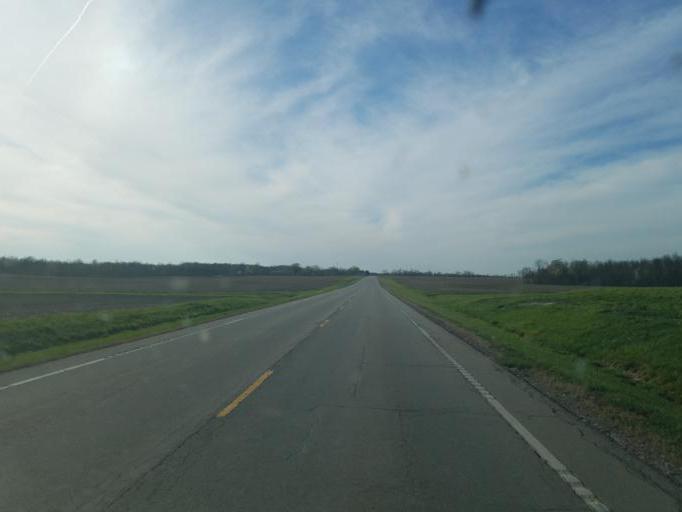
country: US
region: Ohio
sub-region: Huron County
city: New London
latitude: 41.0765
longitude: -82.4635
